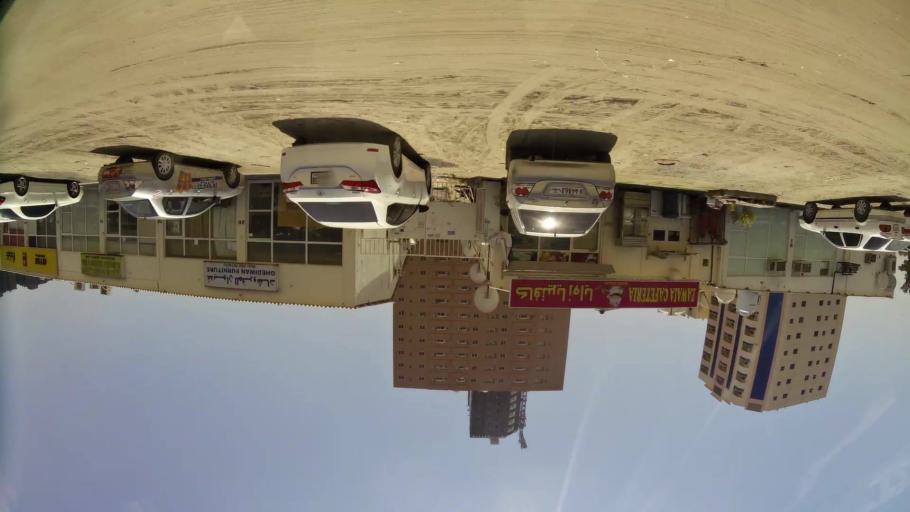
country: AE
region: Ajman
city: Ajman
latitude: 25.3933
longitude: 55.4616
